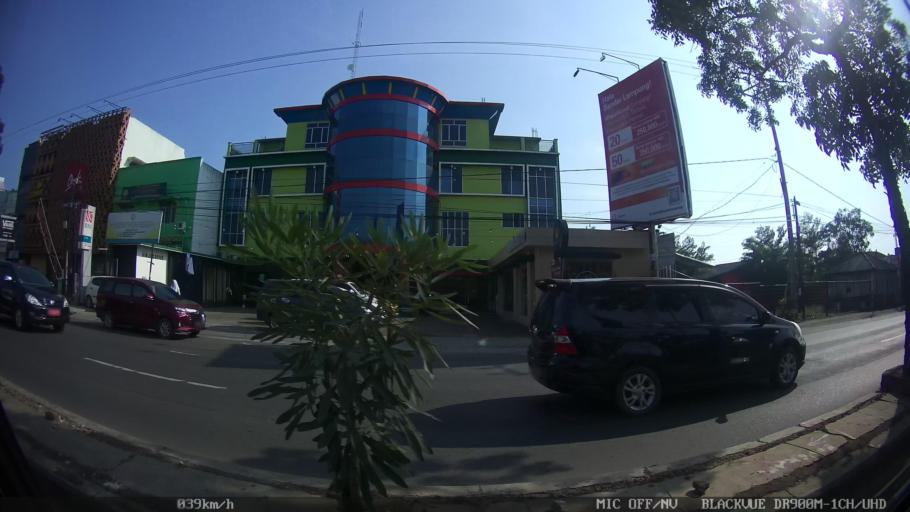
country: ID
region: Lampung
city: Kedaton
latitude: -5.3762
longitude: 105.2482
